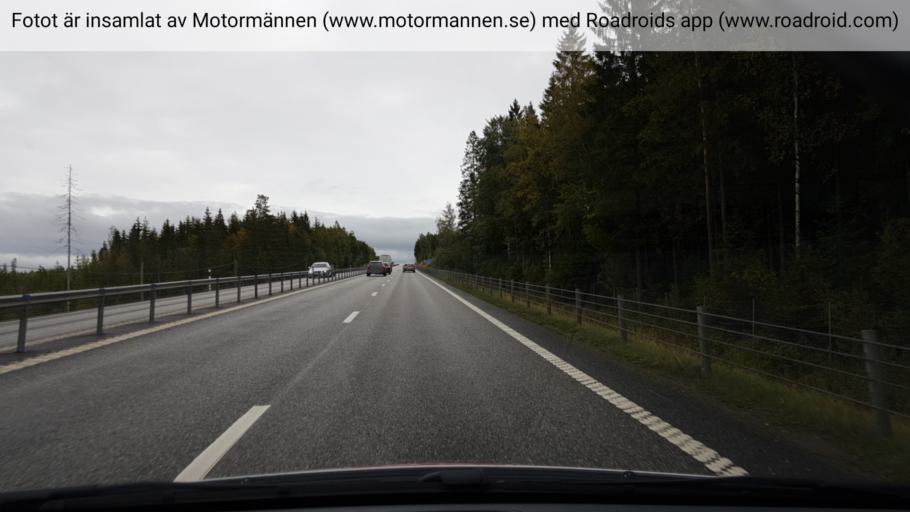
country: SE
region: Vaermland
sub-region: Kristinehamns Kommun
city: Bjorneborg
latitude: 59.3140
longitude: 14.3263
